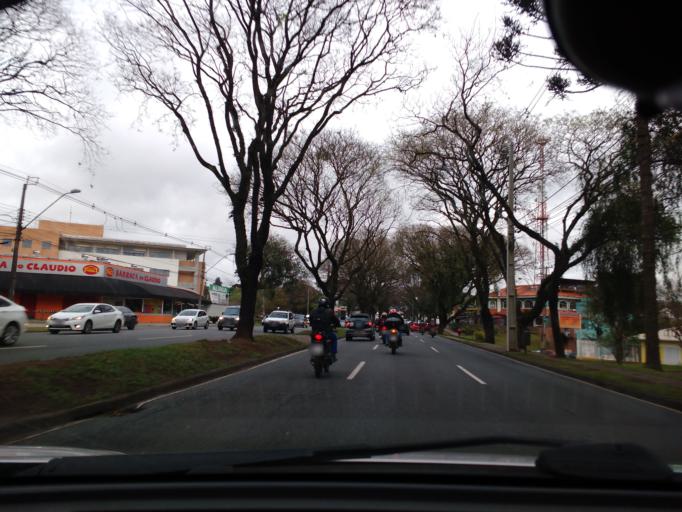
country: BR
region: Parana
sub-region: Curitiba
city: Curitiba
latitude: -25.4277
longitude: -49.2357
